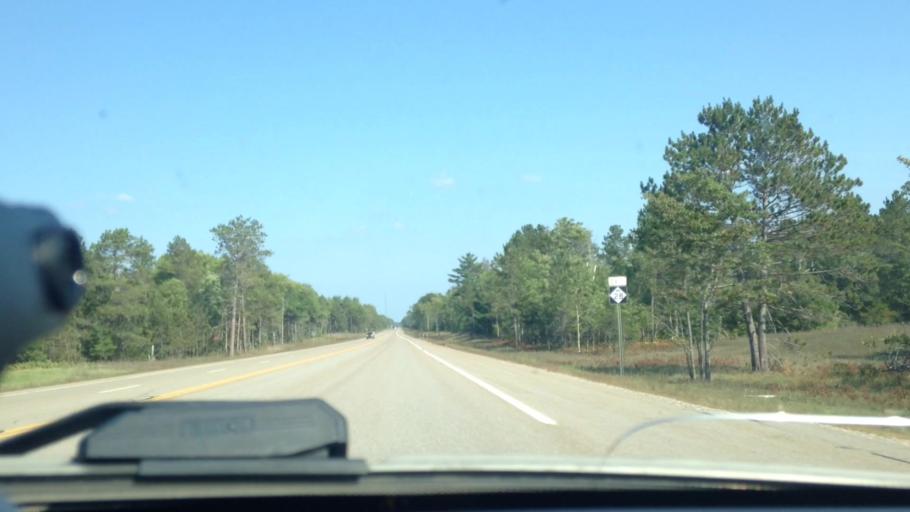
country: US
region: Michigan
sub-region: Chippewa County
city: Sault Ste. Marie
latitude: 46.3651
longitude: -84.7606
